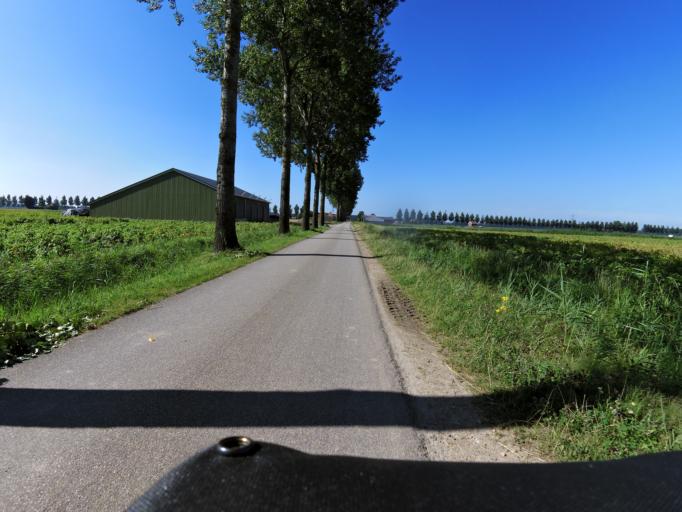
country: NL
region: South Holland
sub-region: Gemeente Dordrecht
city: Dordrecht
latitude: 51.7631
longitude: 4.7177
